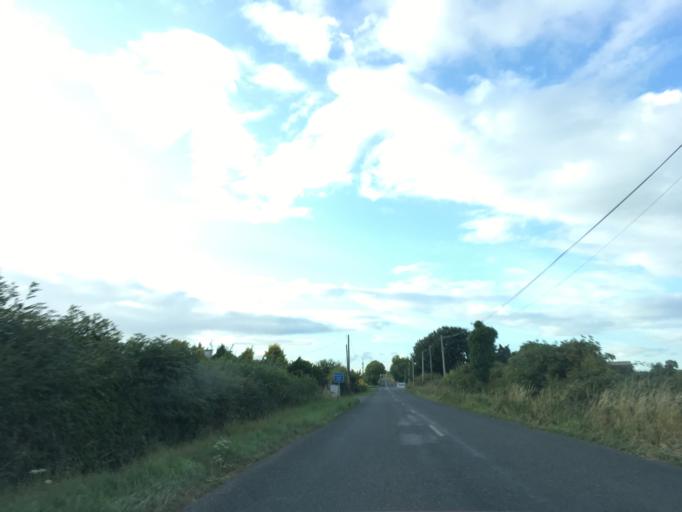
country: IE
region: Munster
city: Cashel
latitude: 52.4641
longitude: -7.9183
